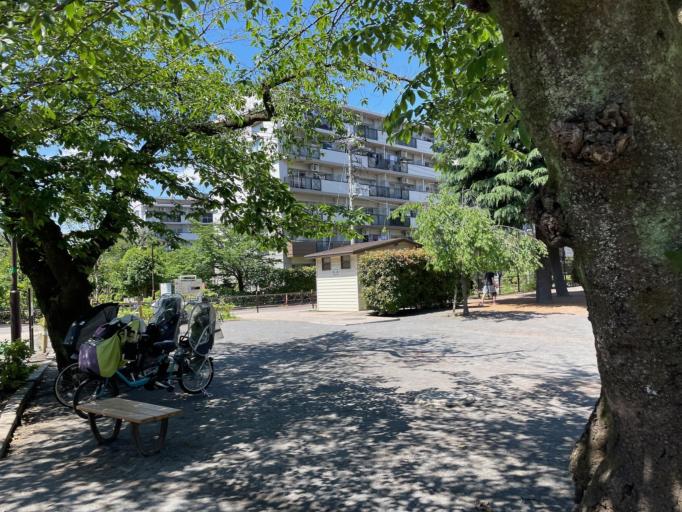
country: JP
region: Tokyo
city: Mitaka-shi
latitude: 35.6549
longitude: 139.6251
